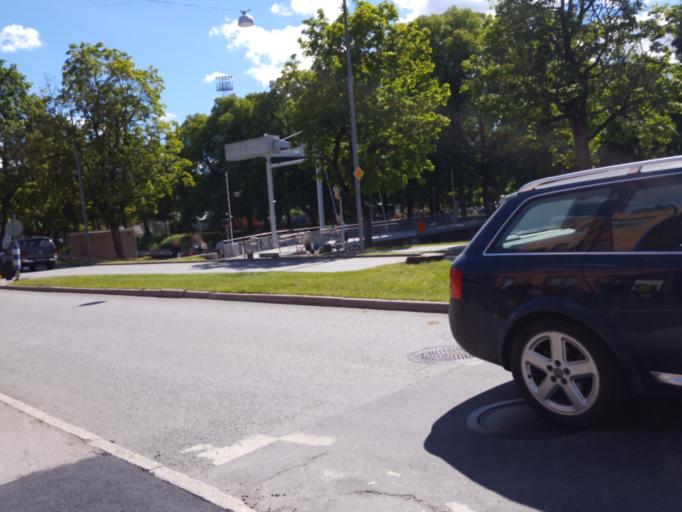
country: SE
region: Uppsala
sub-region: Uppsala Kommun
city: Uppsala
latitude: 59.8522
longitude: 17.6461
